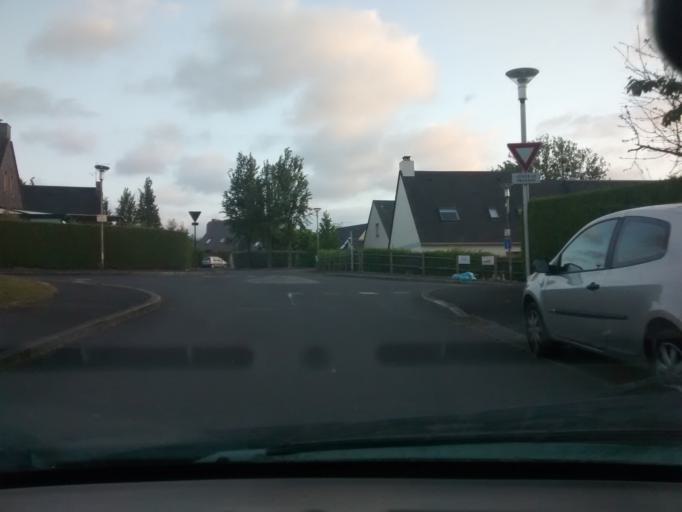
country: FR
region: Lower Normandy
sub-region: Departement de la Manche
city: Saint-Lo
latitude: 49.1036
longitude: -1.0866
